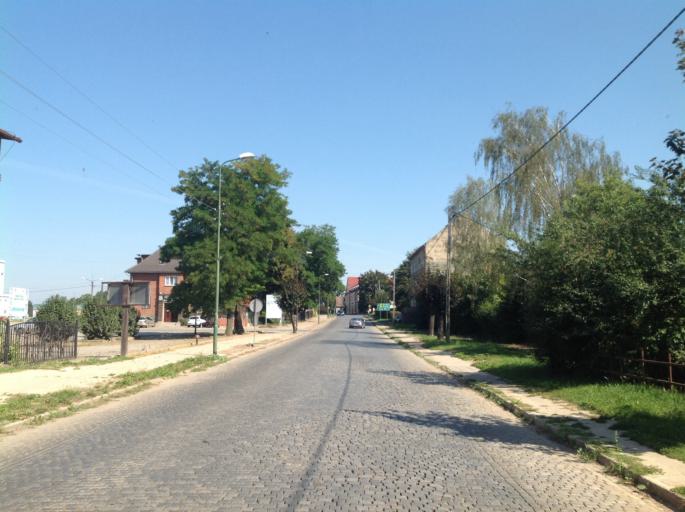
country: PL
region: Lower Silesian Voivodeship
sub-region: Powiat zabkowicki
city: Ziebice
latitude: 50.5937
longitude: 17.0342
